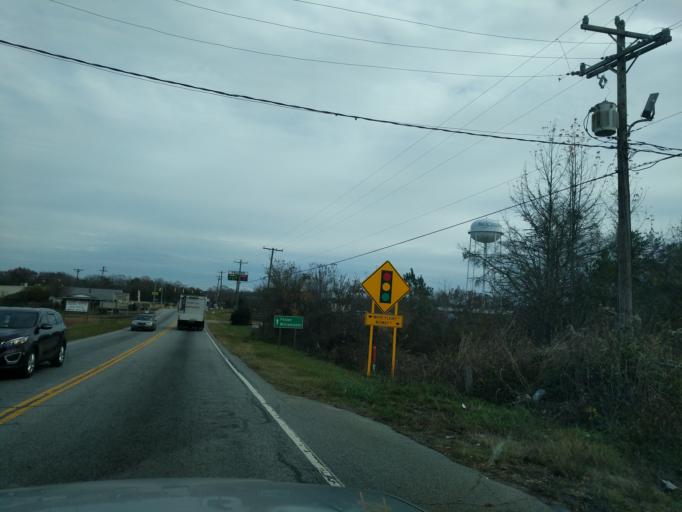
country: US
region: South Carolina
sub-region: Anderson County
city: Piedmont
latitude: 34.6746
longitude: -82.5363
